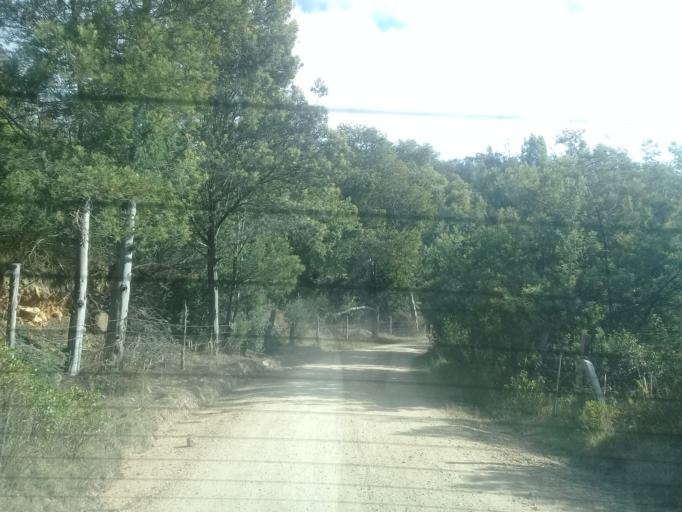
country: CO
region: Cundinamarca
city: Guatavita
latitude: 4.9423
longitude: -73.8685
